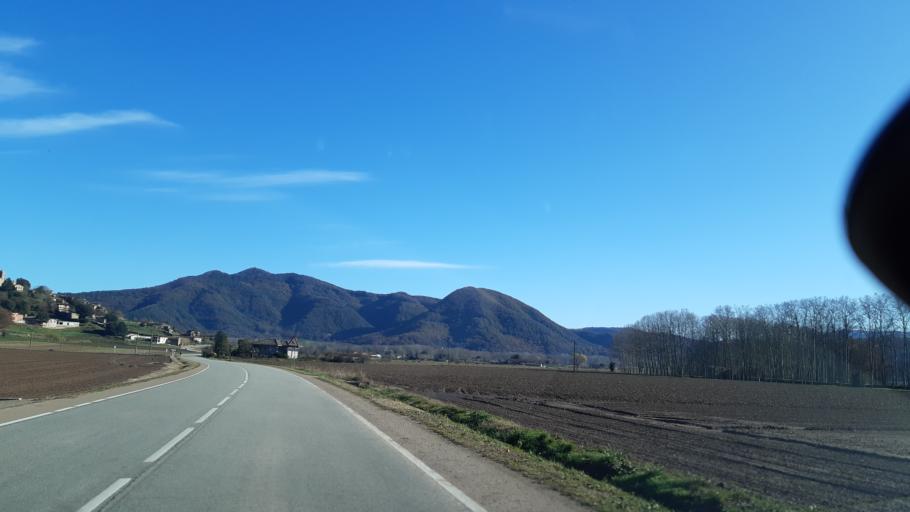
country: ES
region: Catalonia
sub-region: Provincia de Girona
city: Bas
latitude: 42.1496
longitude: 2.4278
